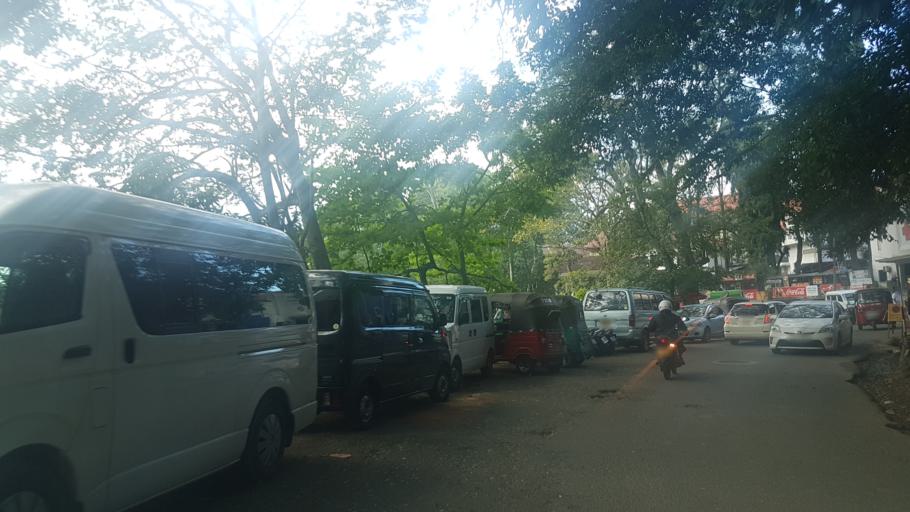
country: LK
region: Central
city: Kandy
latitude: 7.2908
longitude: 80.6437
